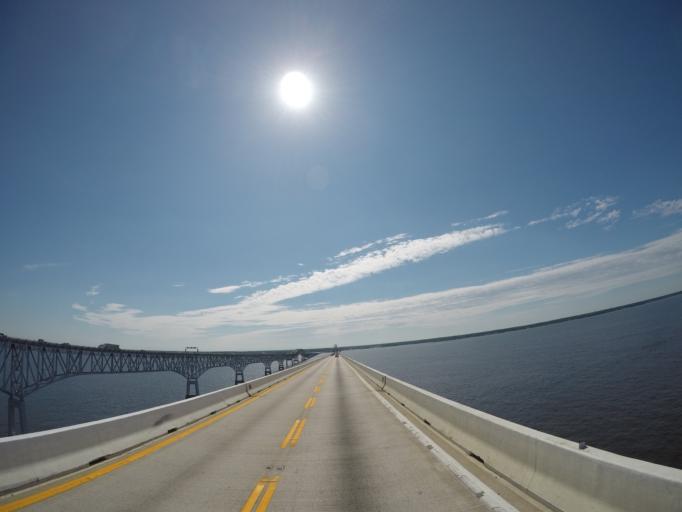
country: US
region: Maryland
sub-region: Queen Anne's County
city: Stevensville
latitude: 38.9907
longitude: -76.3715
